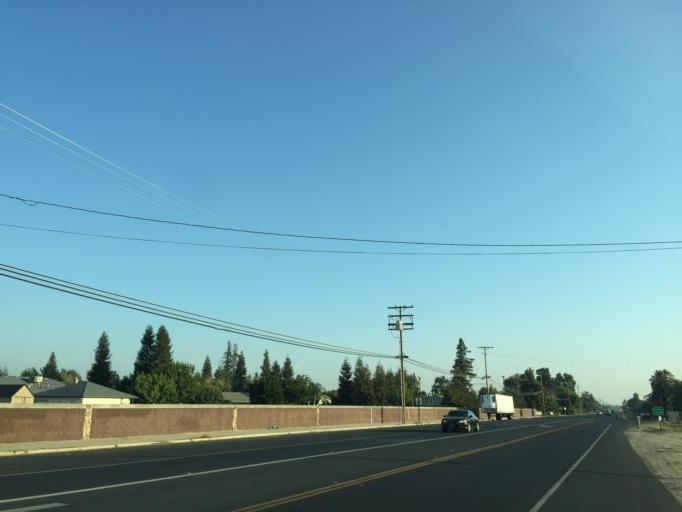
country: US
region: California
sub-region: Tulare County
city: Visalia
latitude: 36.3710
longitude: -119.2968
